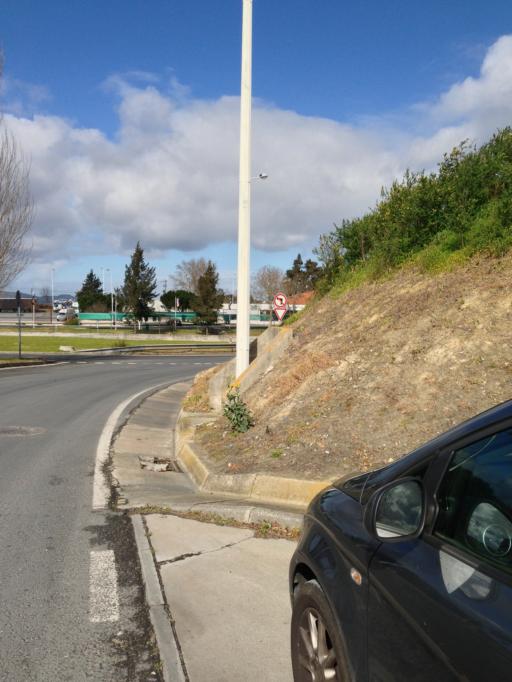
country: PT
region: Lisbon
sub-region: Azambuja
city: Aveiras de Cima
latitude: 39.1227
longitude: -8.9070
